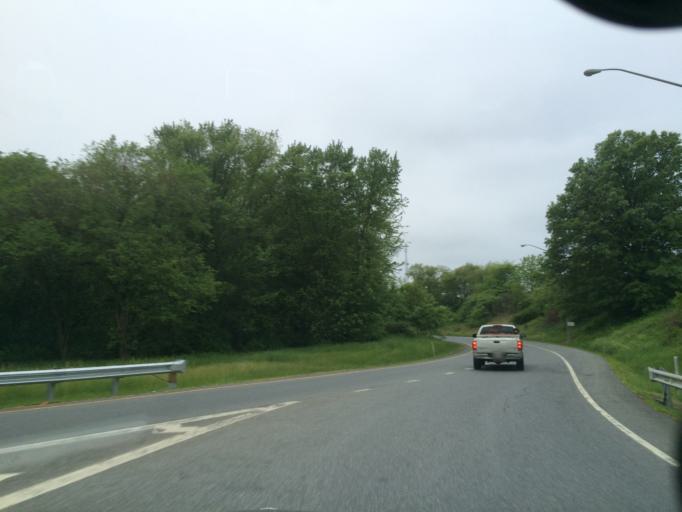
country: US
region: Maryland
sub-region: Washington County
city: Halfway
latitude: 39.6074
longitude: -77.7295
